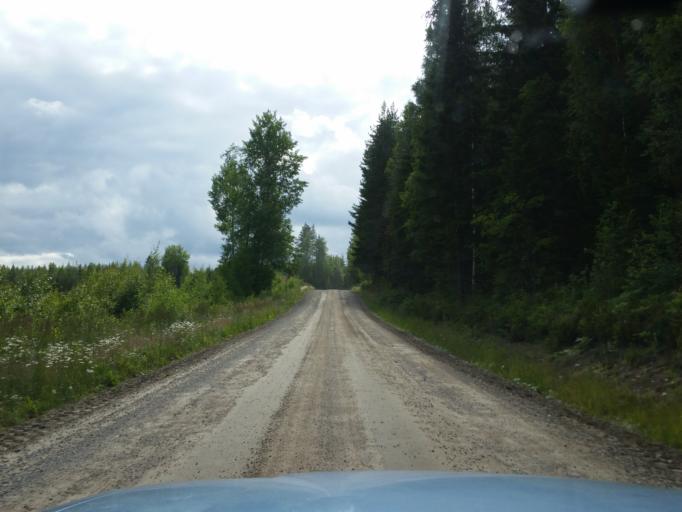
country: FI
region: Southern Savonia
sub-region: Savonlinna
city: Sulkava
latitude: 61.7367
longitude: 28.3333
